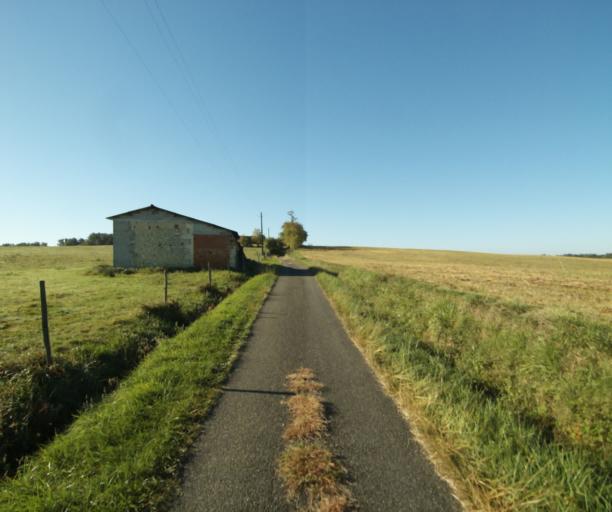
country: FR
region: Midi-Pyrenees
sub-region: Departement du Gers
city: Gondrin
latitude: 43.8457
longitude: 0.2243
